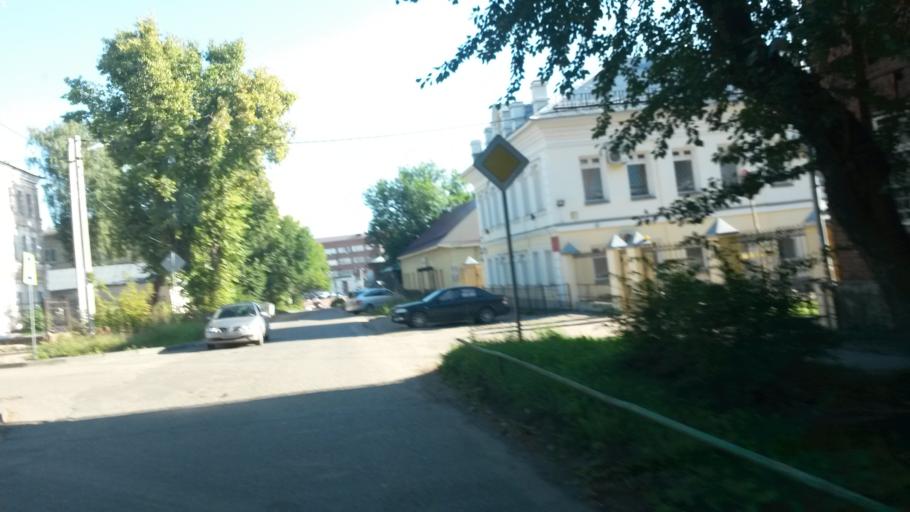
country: RU
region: Ivanovo
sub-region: Gorod Ivanovo
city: Ivanovo
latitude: 56.9920
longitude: 40.9785
